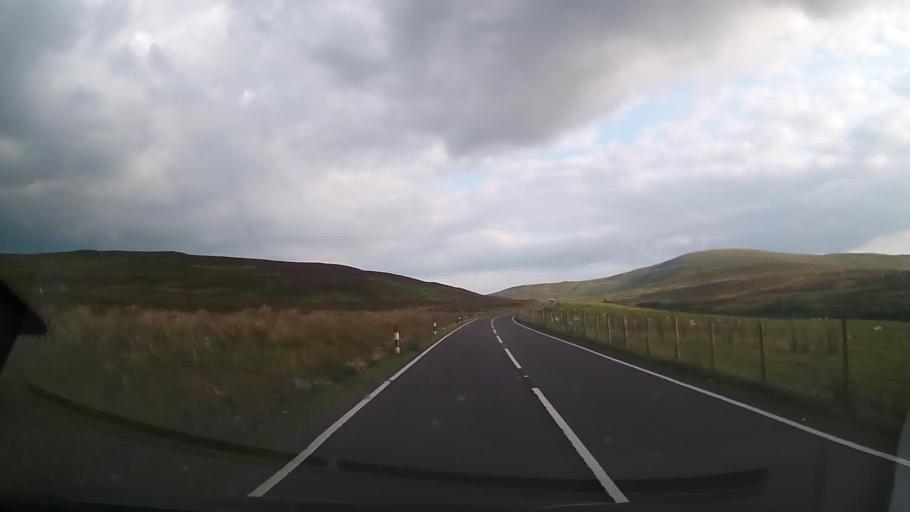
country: GB
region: Wales
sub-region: Denbighshire
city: Llandrillo
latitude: 52.8937
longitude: -3.4866
